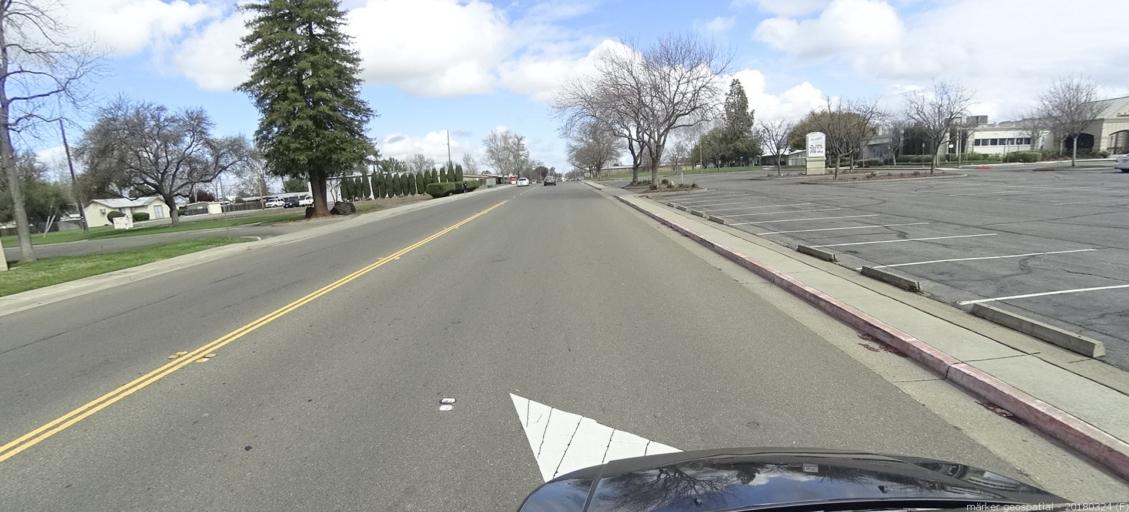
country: US
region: California
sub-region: Sacramento County
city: North Highlands
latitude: 38.6695
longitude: -121.3875
